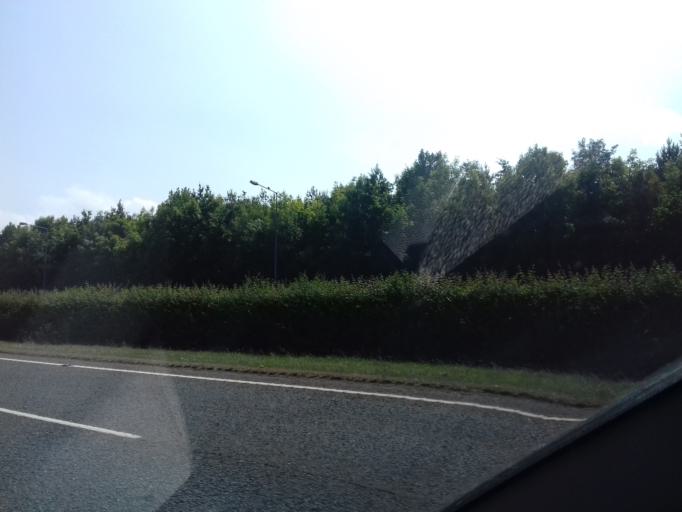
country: IE
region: Leinster
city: Balrothery
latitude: 53.5941
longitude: -6.2161
